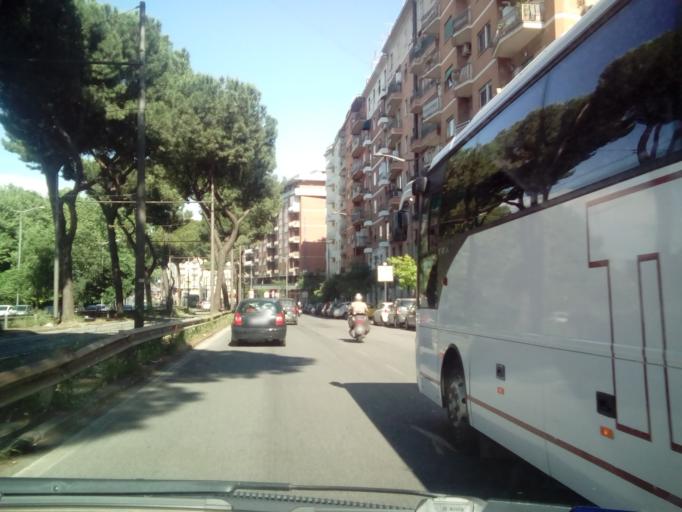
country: IT
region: Latium
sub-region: Citta metropolitana di Roma Capitale
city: Rome
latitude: 41.8924
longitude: 12.5379
